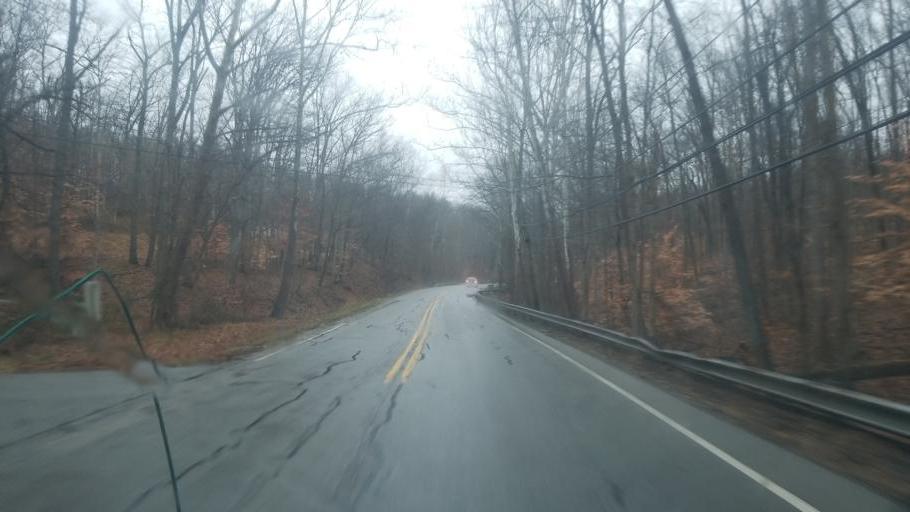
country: US
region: Indiana
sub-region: Brown County
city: Nashville
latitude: 39.1973
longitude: -86.2513
